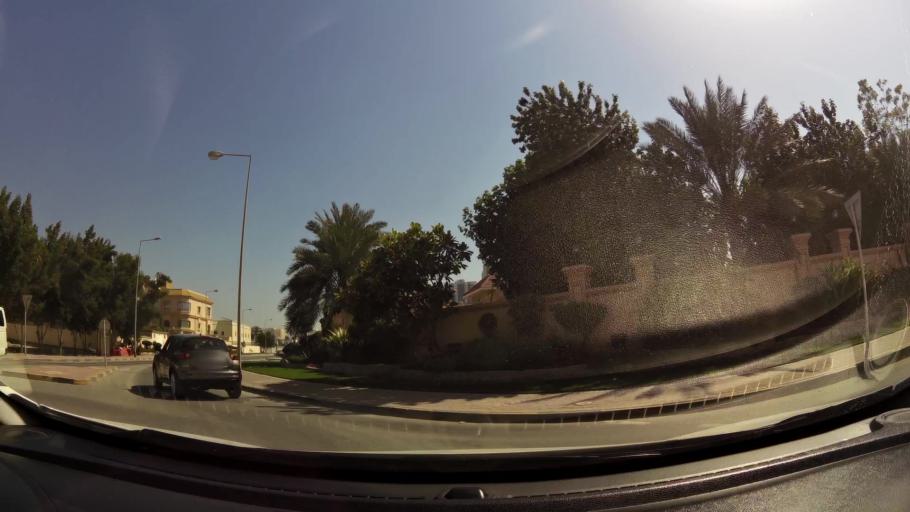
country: BH
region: Manama
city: Manama
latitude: 26.2108
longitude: 50.5789
